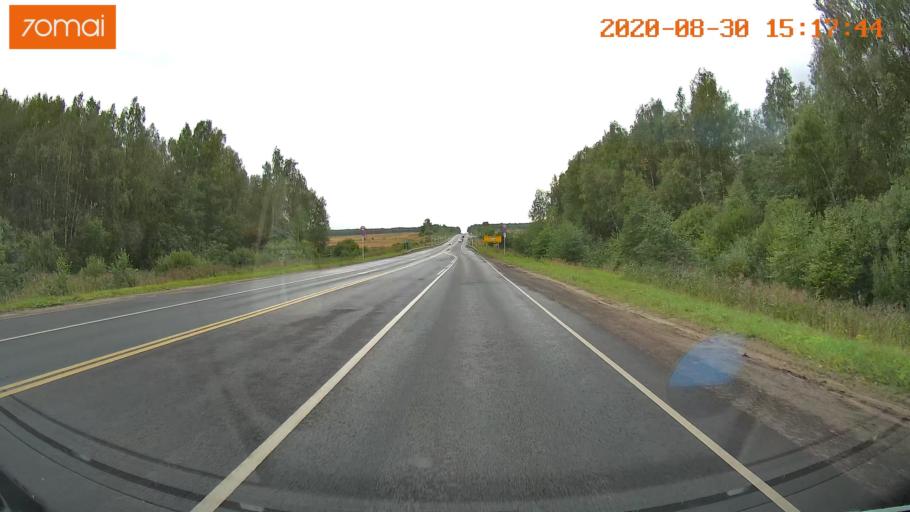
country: RU
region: Ivanovo
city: Rodniki
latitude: 57.1312
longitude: 41.8010
